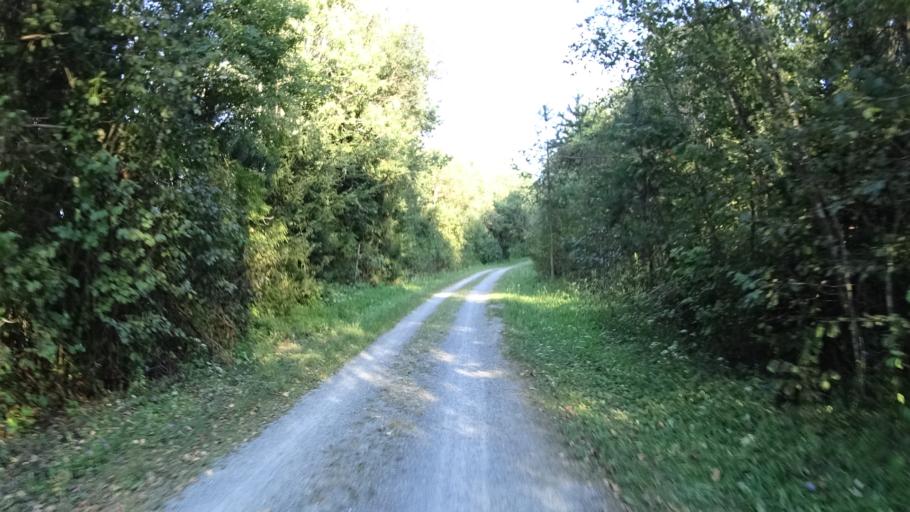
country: AT
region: Carinthia
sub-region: Politischer Bezirk Villach Land
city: Rosegg
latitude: 46.5736
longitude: 14.0487
